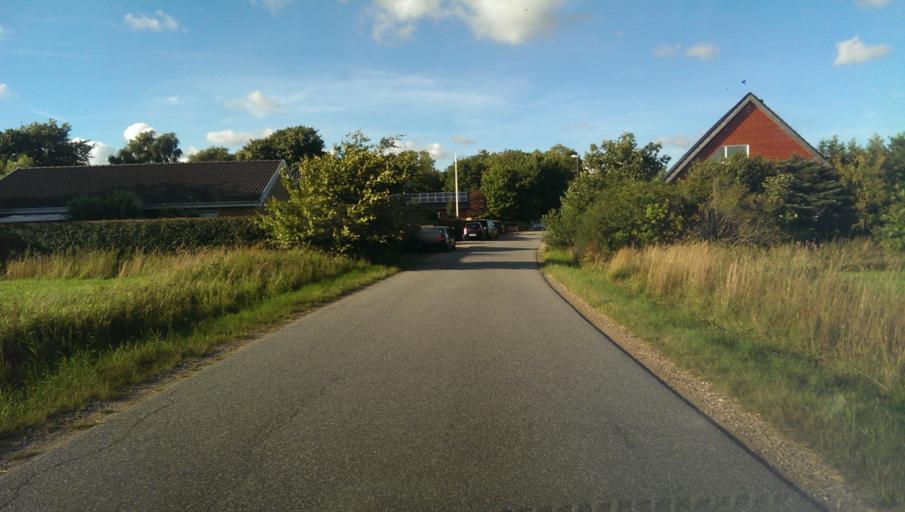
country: DK
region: South Denmark
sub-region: Esbjerg Kommune
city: Tjaereborg
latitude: 55.5043
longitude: 8.5564
